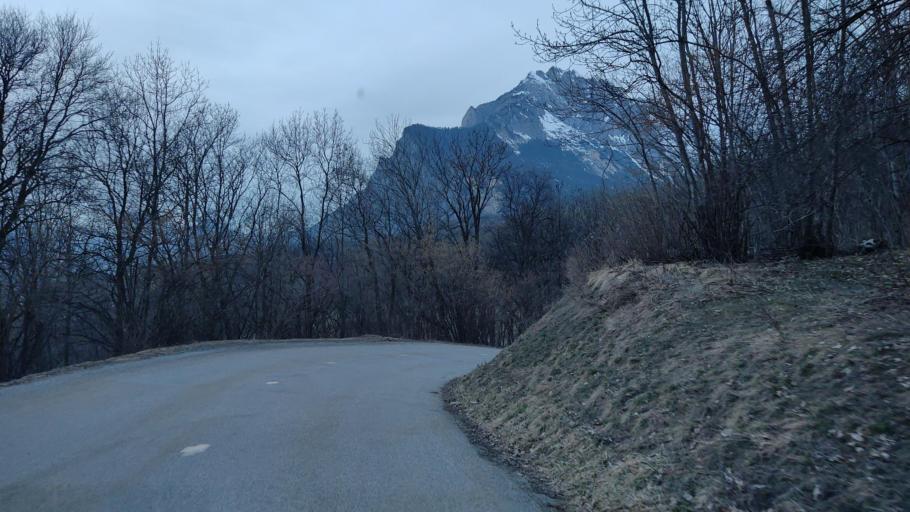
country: FR
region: Rhone-Alpes
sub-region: Departement de la Savoie
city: Saint-Michel-de-Maurienne
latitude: 45.2299
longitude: 6.4731
